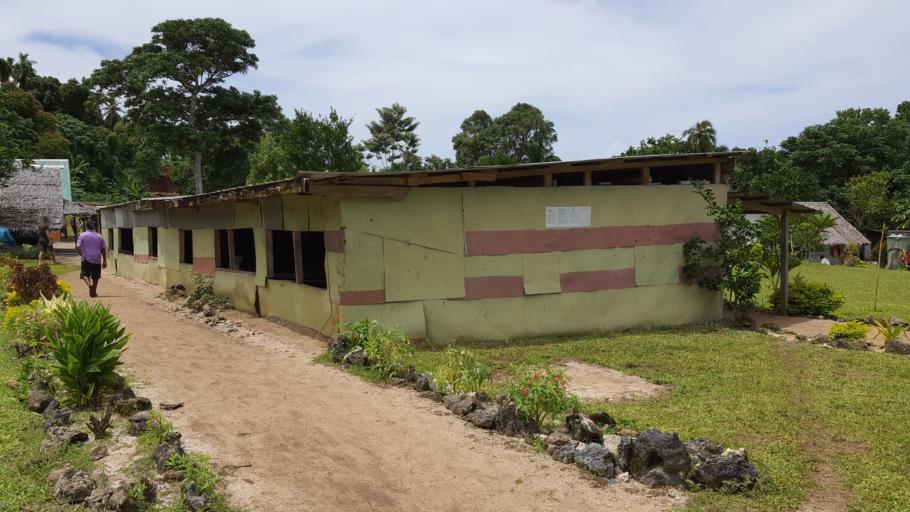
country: VU
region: Malampa
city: Lakatoro
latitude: -16.5008
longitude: 167.6497
